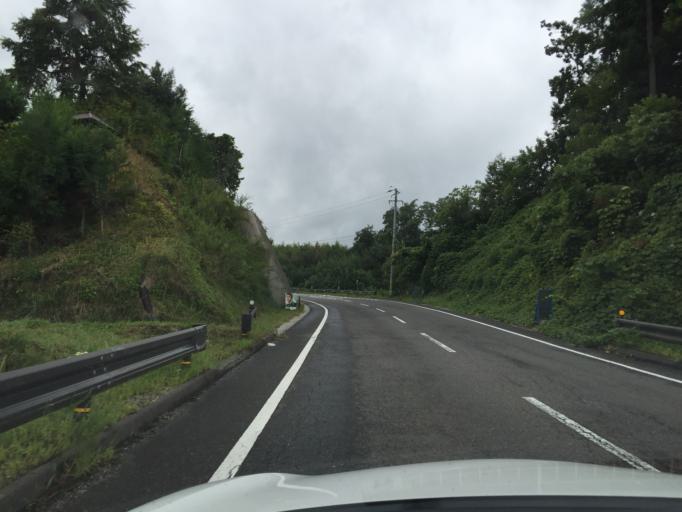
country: JP
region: Fukushima
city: Miharu
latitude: 37.4544
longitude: 140.5260
